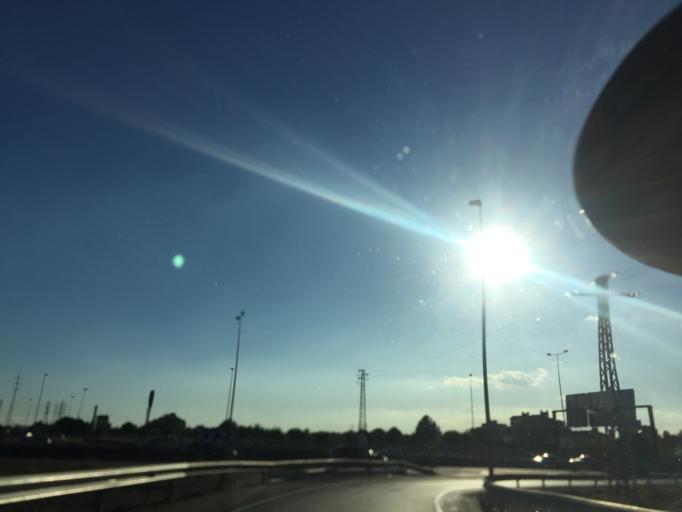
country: ES
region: Andalusia
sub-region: Provincia de Sevilla
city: Sevilla
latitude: 37.3607
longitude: -5.9564
